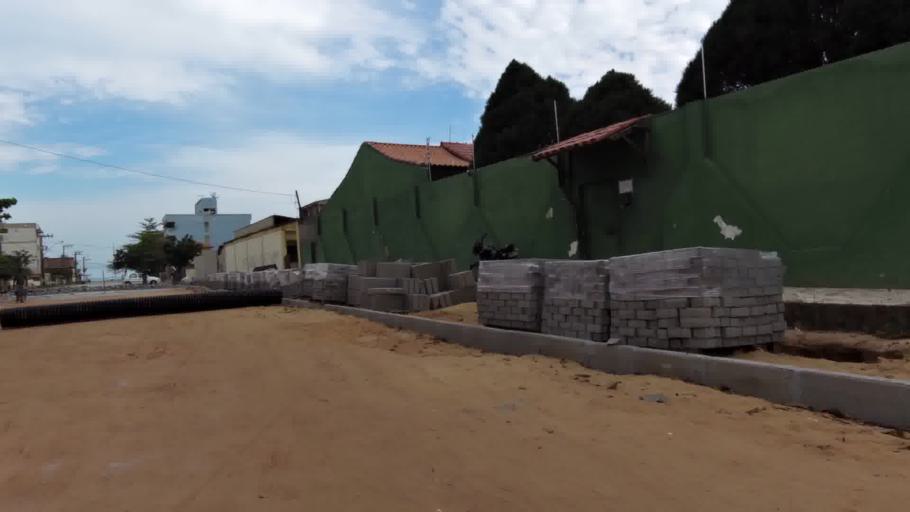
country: BR
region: Espirito Santo
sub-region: Piuma
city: Piuma
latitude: -20.8418
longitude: -40.7358
